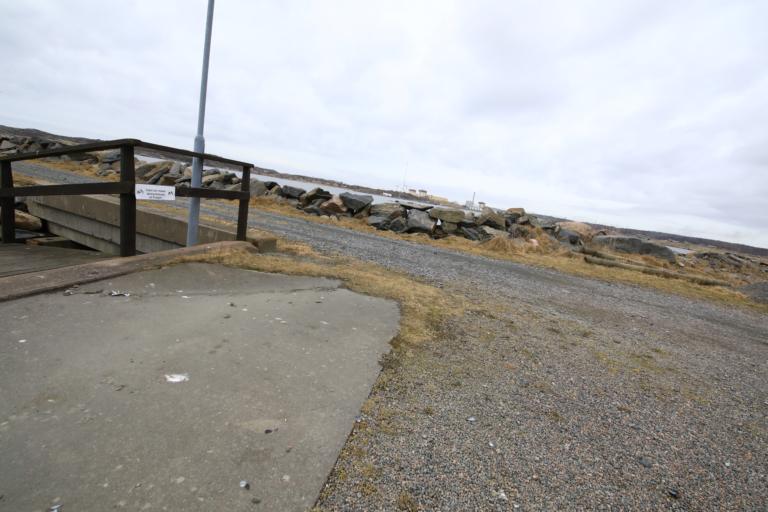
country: SE
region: Halland
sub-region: Kungsbacka Kommun
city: Frillesas
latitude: 57.2428
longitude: 12.1152
